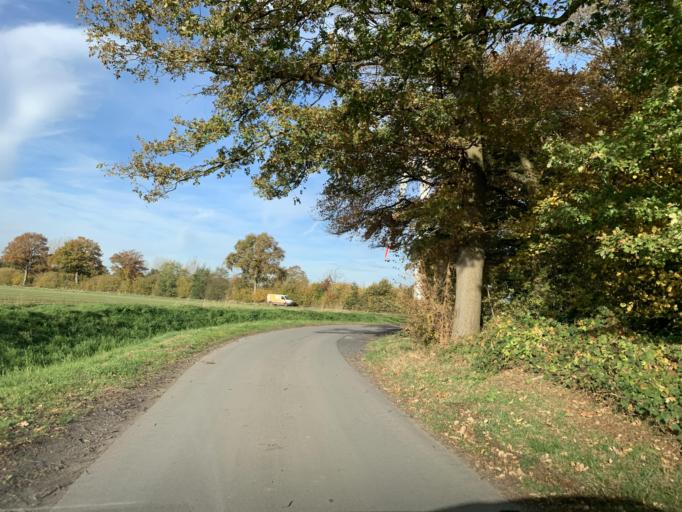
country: DE
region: North Rhine-Westphalia
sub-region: Regierungsbezirk Munster
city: Muenster
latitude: 52.0188
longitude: 7.6079
